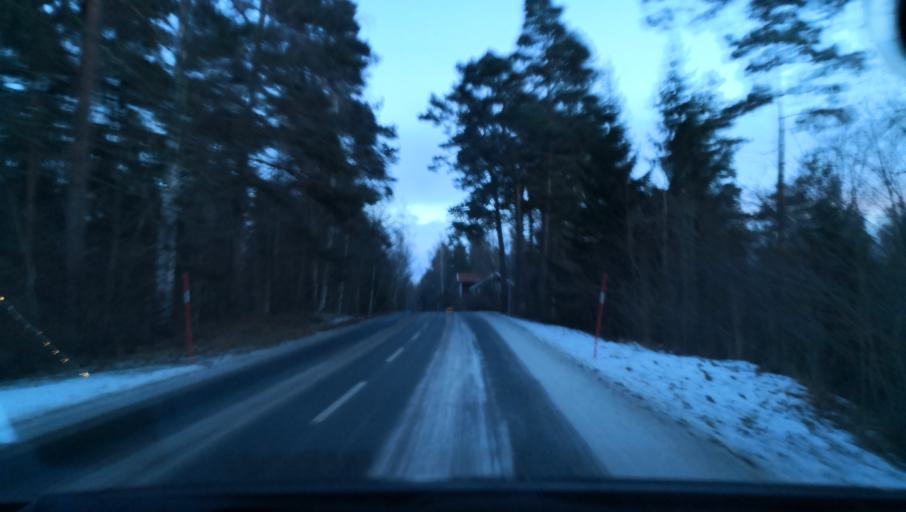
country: SE
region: Soedermanland
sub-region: Katrineholms Kommun
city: Katrineholm
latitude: 59.0856
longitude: 16.2178
